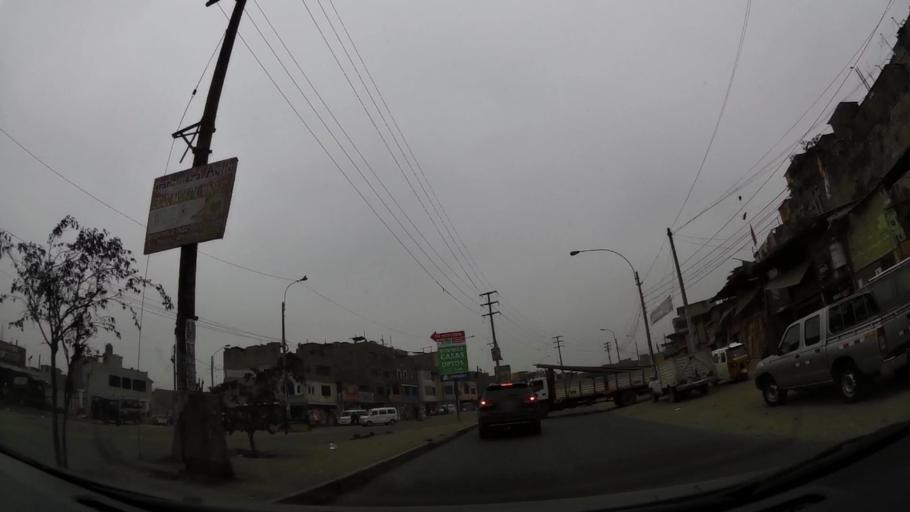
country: PE
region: Lima
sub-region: Lima
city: Urb. Santo Domingo
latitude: -11.8819
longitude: -77.0232
